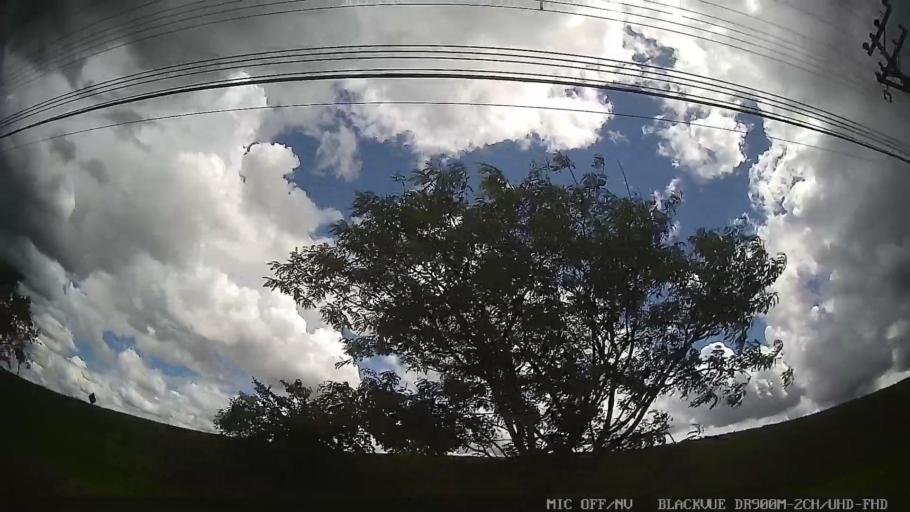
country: BR
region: Sao Paulo
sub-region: Jaguariuna
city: Jaguariuna
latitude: -22.6936
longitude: -47.0116
